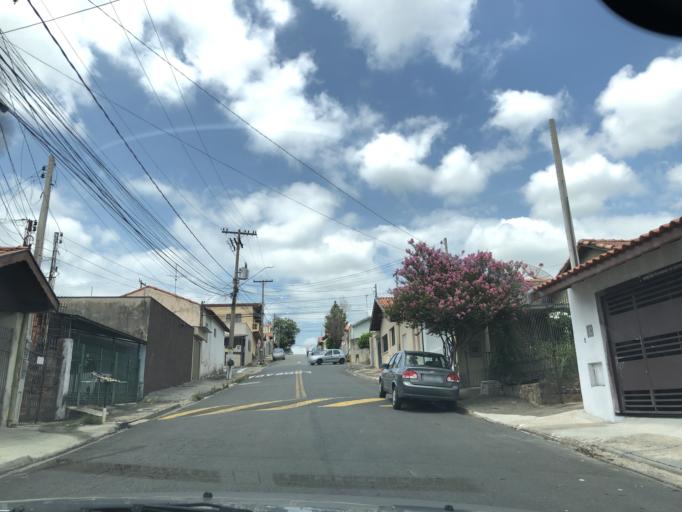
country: BR
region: Sao Paulo
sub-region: Piracicaba
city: Piracicaba
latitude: -22.7496
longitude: -47.6515
